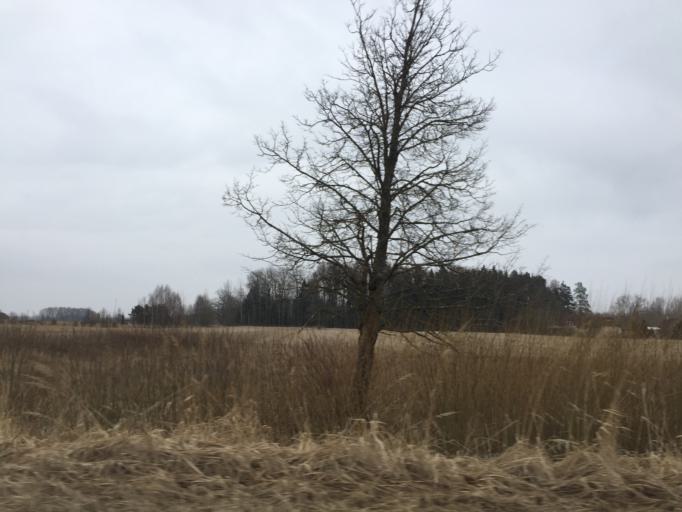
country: LV
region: Lielvarde
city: Lielvarde
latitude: 56.7352
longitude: 24.8198
